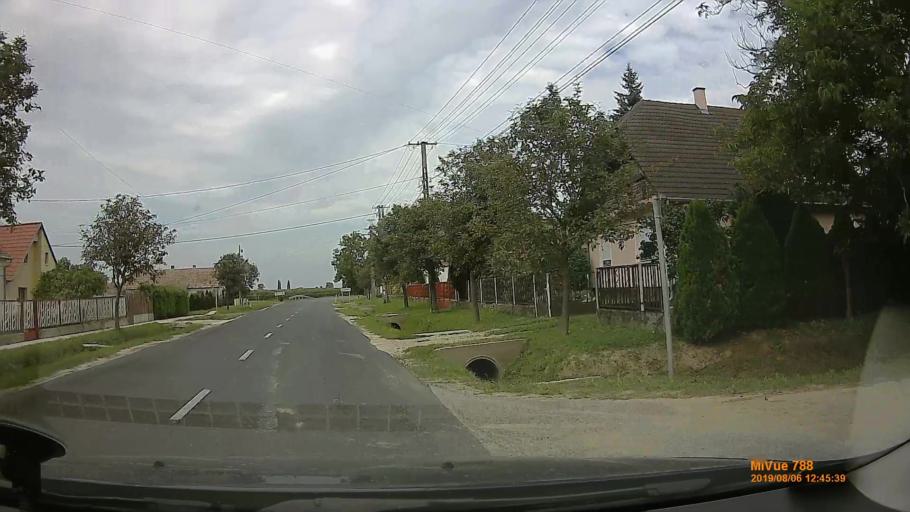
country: HU
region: Zala
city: Nagykanizsa
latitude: 46.5696
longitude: 16.9883
